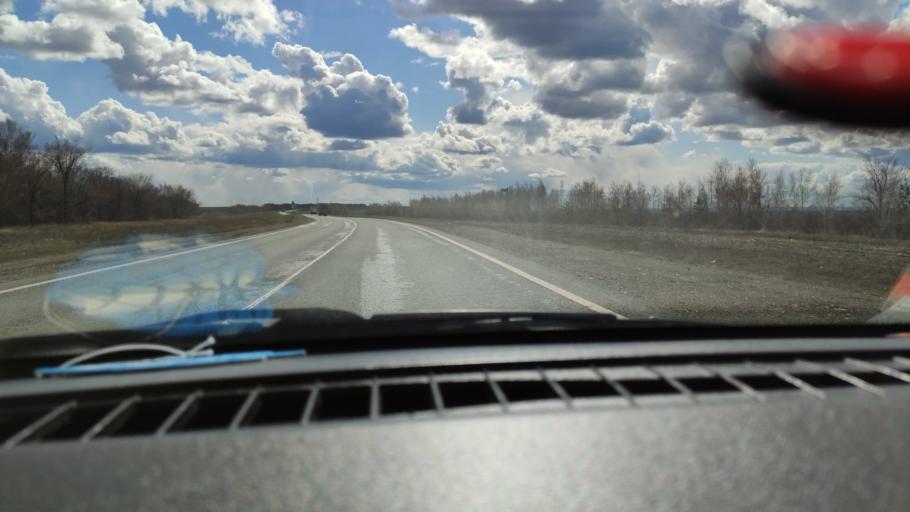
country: RU
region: Samara
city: Syzran'
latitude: 52.8544
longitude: 48.2592
